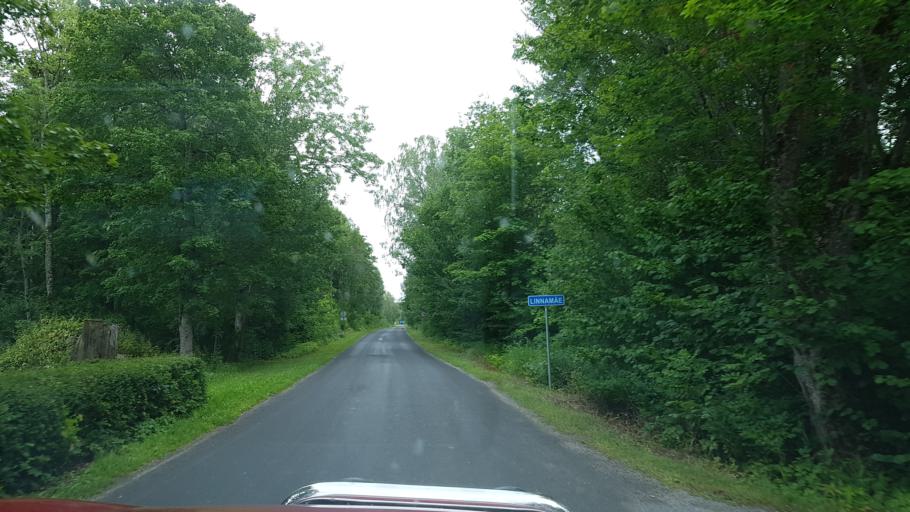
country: EE
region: Laeaene
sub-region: Ridala Parish
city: Uuemoisa
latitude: 59.0011
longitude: 23.7216
